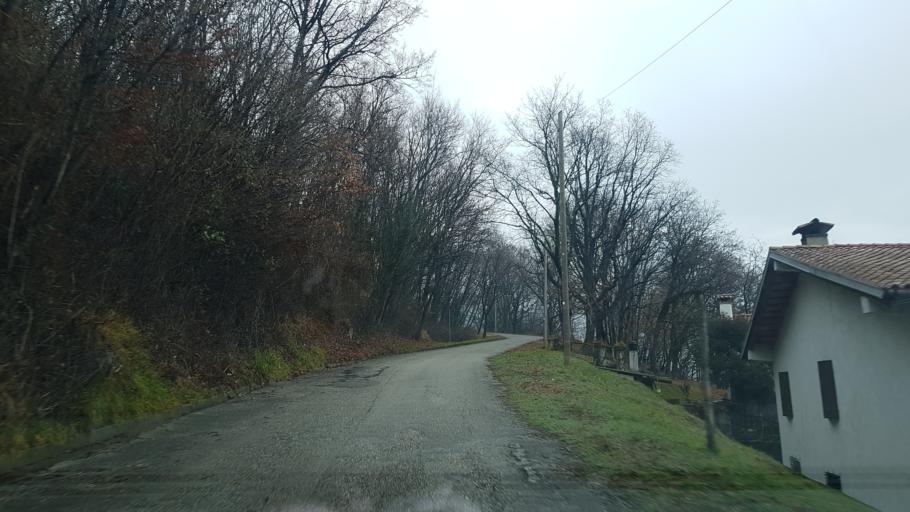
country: IT
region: Friuli Venezia Giulia
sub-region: Provincia di Udine
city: San Pietro al Natisone
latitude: 46.0806
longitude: 13.4822
